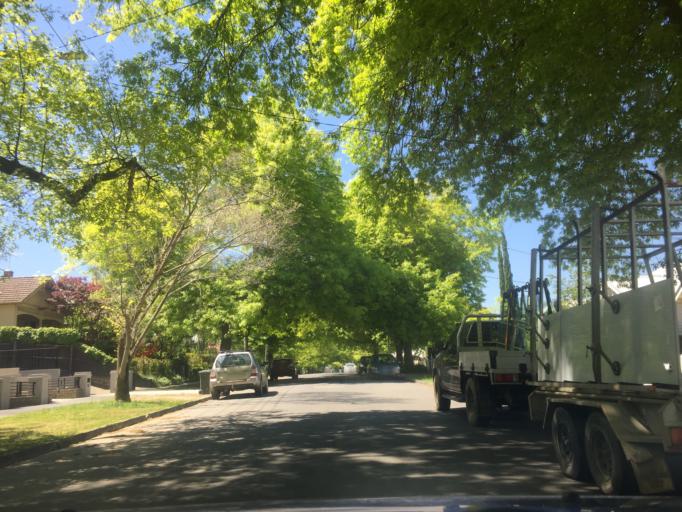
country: AU
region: Victoria
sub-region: Boroondara
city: Canterbury
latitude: -37.8231
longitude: 145.0916
